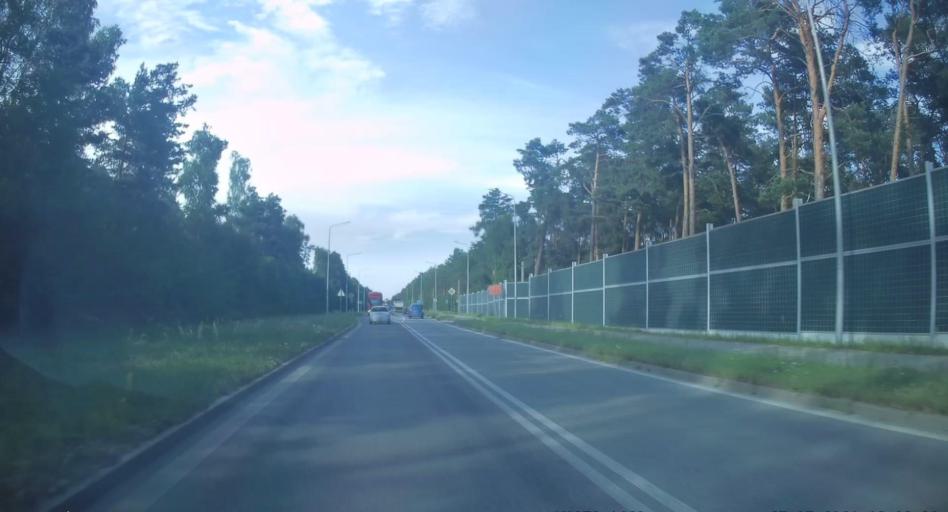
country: PL
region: Swietokrzyskie
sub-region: Powiat konecki
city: Konskie
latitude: 51.1214
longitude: 20.3541
